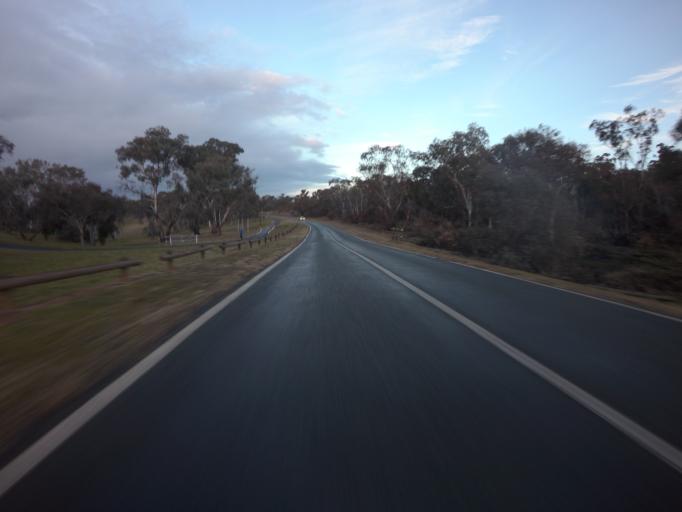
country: AU
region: Australian Capital Territory
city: Acton
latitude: -35.2995
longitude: 149.1108
